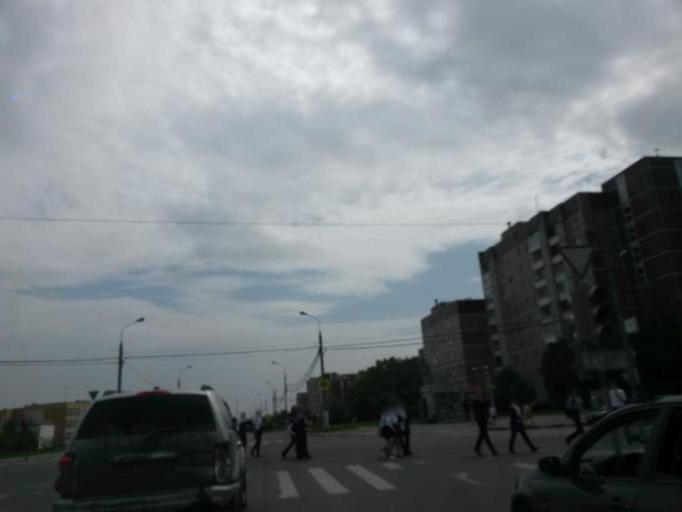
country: RU
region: Moskovskaya
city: Shcherbinka
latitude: 55.5382
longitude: 37.5339
